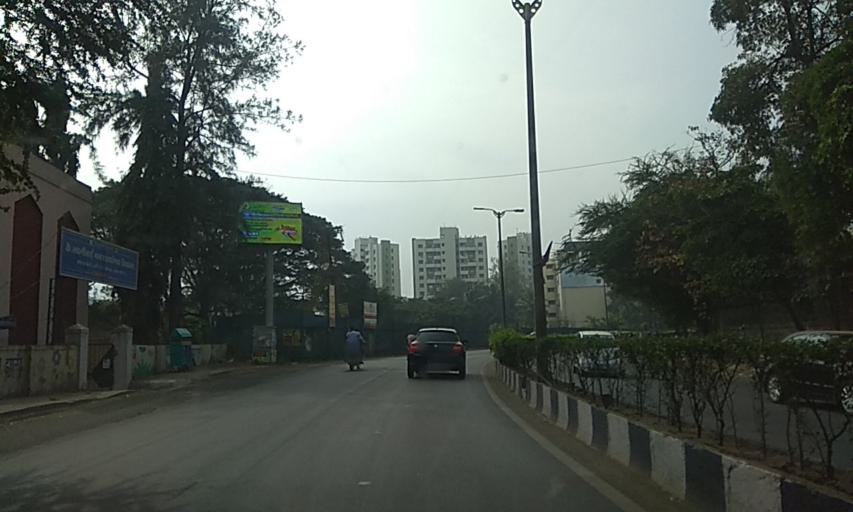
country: IN
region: Maharashtra
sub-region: Pune Division
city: Pune
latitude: 18.5117
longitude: 73.9324
